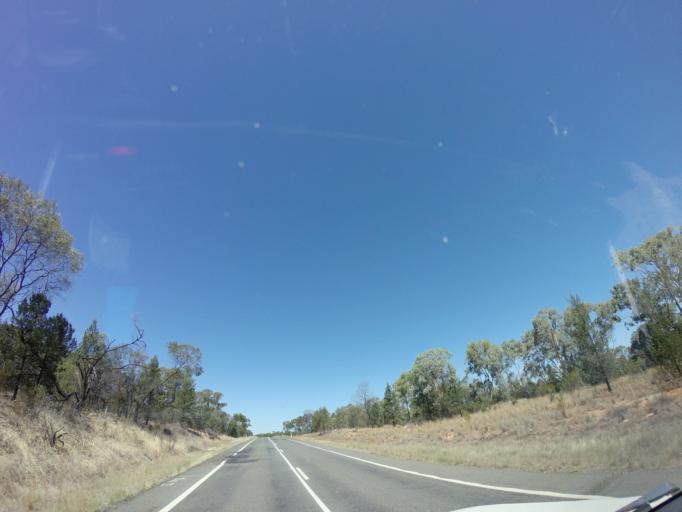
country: AU
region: New South Wales
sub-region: Bogan
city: Nyngan
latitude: -31.5496
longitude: 146.6920
